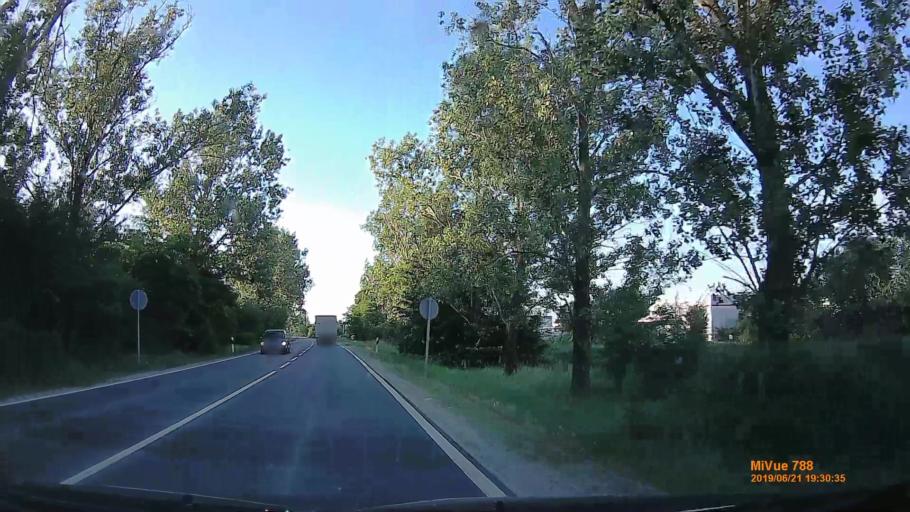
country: HU
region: Pest
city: Szazhalombatta
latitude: 47.3202
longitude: 18.8911
